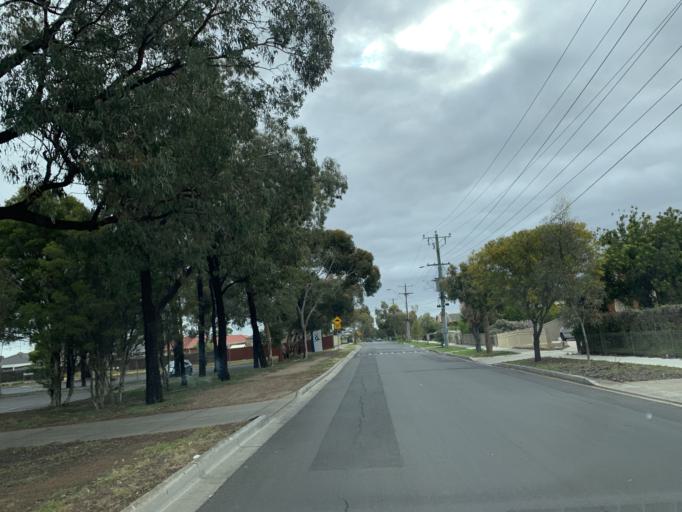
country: AU
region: Victoria
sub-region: Brimbank
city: St Albans
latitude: -37.7479
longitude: 144.7984
